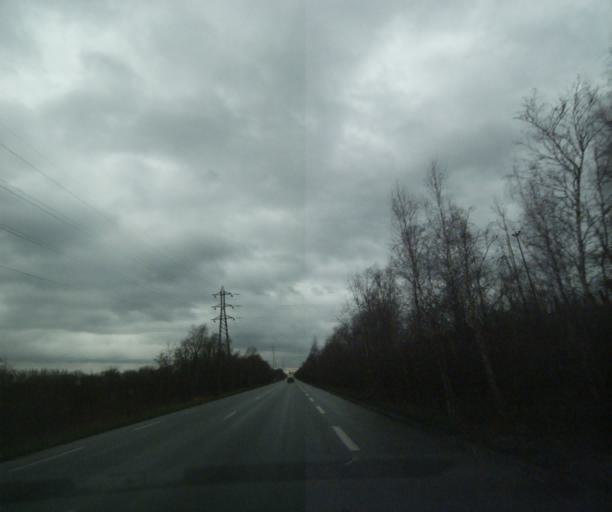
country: FR
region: Nord-Pas-de-Calais
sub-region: Departement du Nord
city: Bruay-sur-l'Escaut
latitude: 50.3964
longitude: 3.5692
